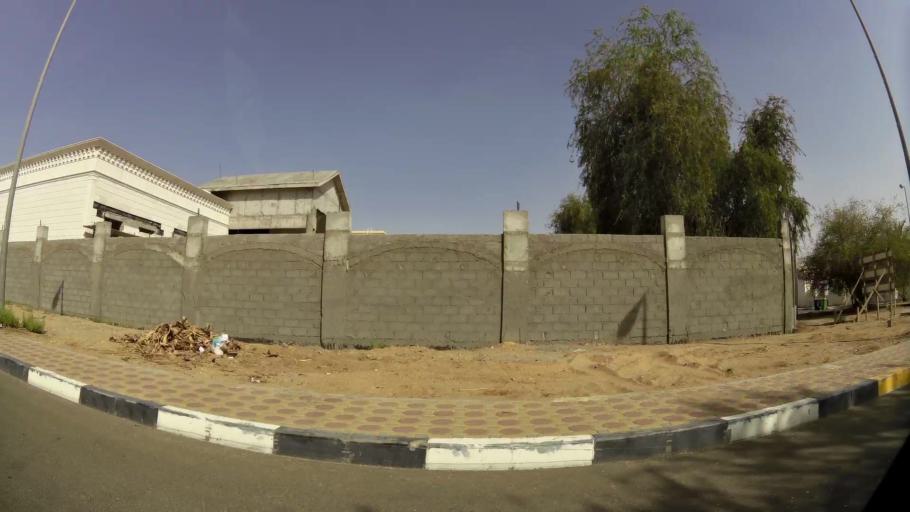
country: AE
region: Abu Dhabi
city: Al Ain
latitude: 24.2470
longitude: 55.6845
